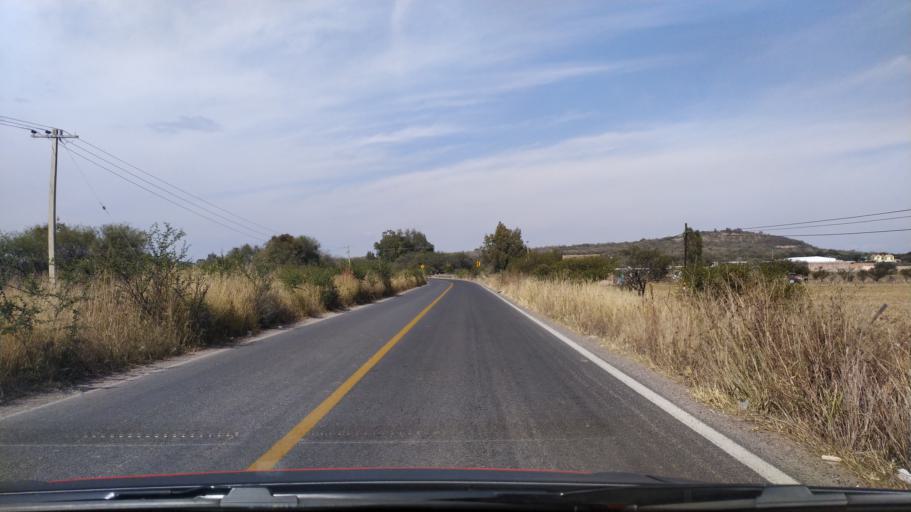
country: MX
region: Guanajuato
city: Ciudad Manuel Doblado
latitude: 20.7954
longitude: -101.9845
